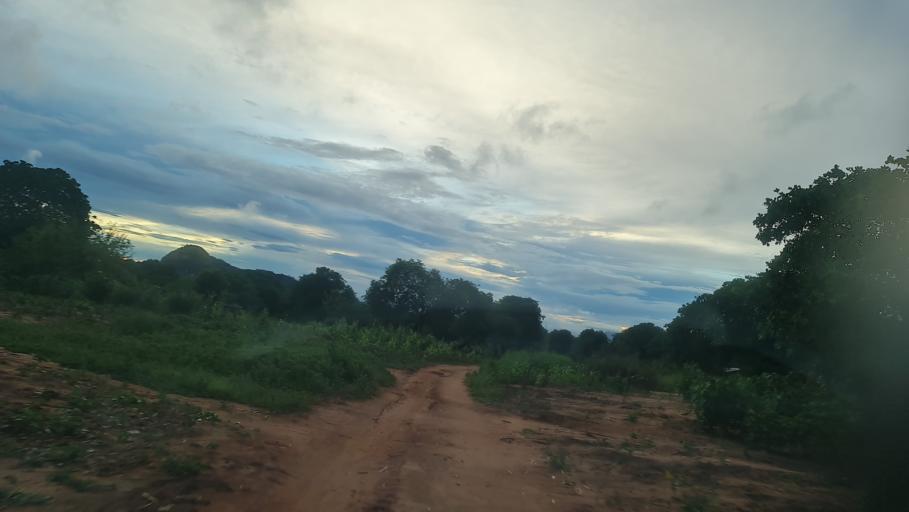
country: MZ
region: Nampula
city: Nampula
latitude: -14.7408
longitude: 39.9359
